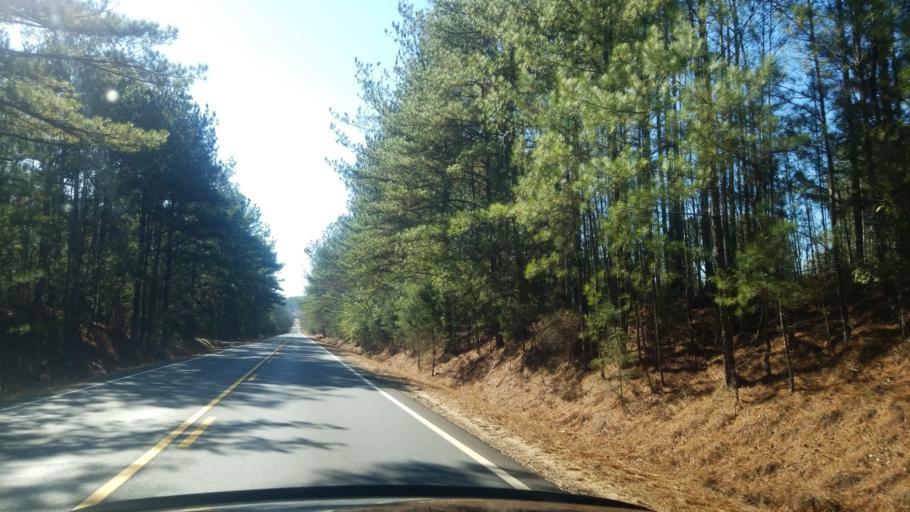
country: US
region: Alabama
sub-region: Chambers County
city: Valley
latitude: 32.8033
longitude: -85.1030
